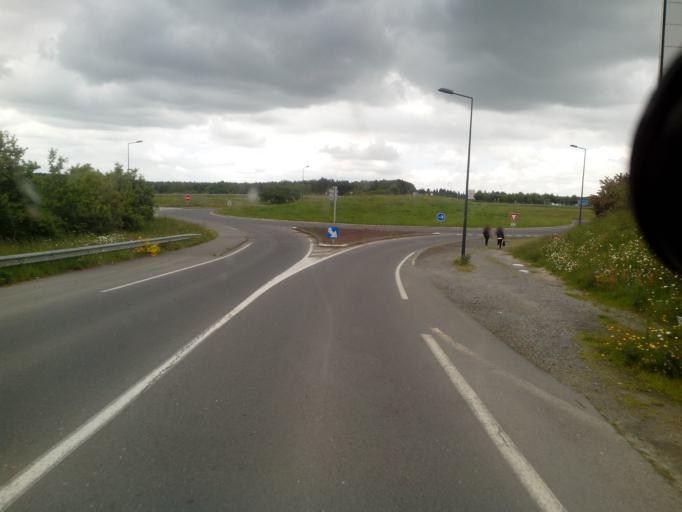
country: FR
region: Brittany
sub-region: Departement d'Ille-et-Vilaine
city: Liffre
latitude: 48.2201
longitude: -1.4977
